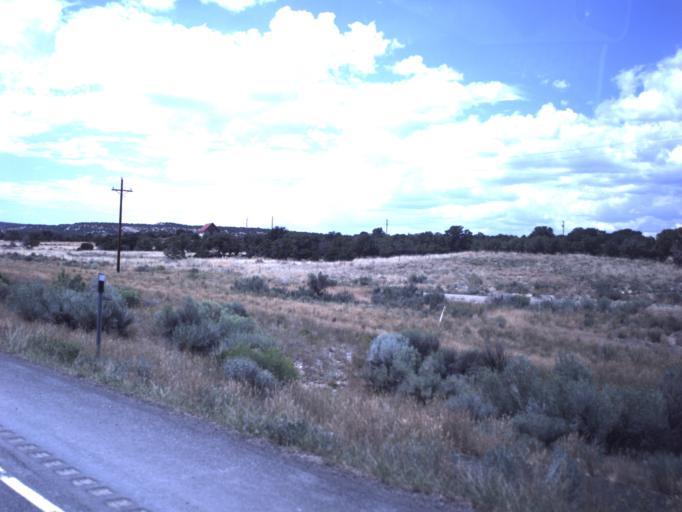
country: US
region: Utah
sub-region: Duchesne County
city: Duchesne
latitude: 40.1781
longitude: -110.5339
